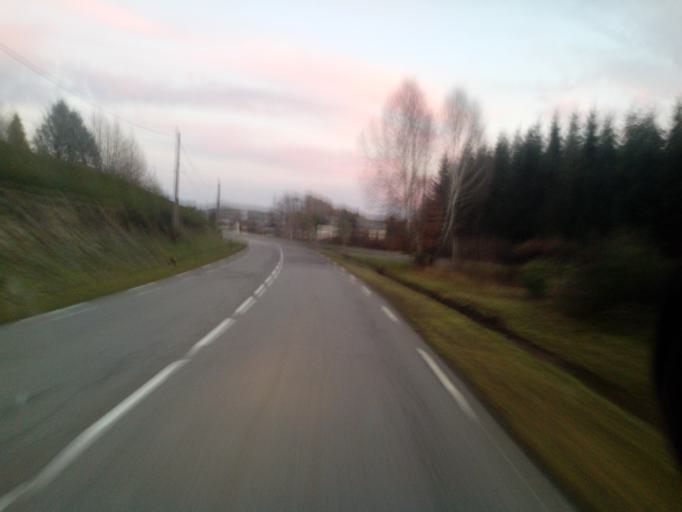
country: FR
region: Limousin
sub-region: Departement de la Correze
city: Meymac
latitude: 45.5032
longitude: 2.2187
